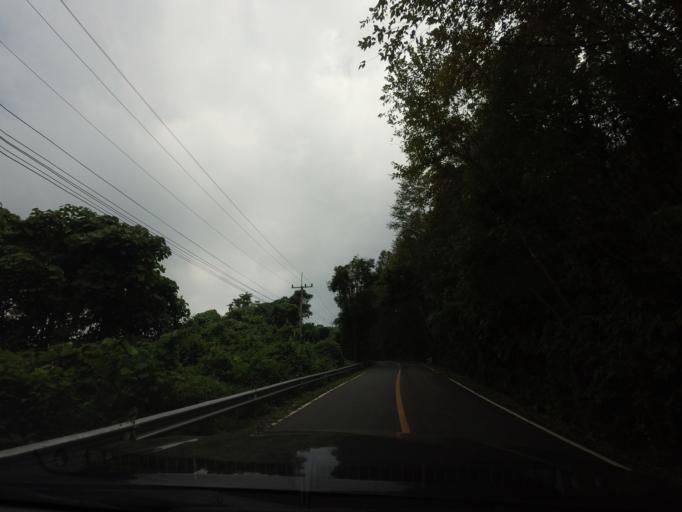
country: TH
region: Nan
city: Pua
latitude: 19.1889
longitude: 101.0195
